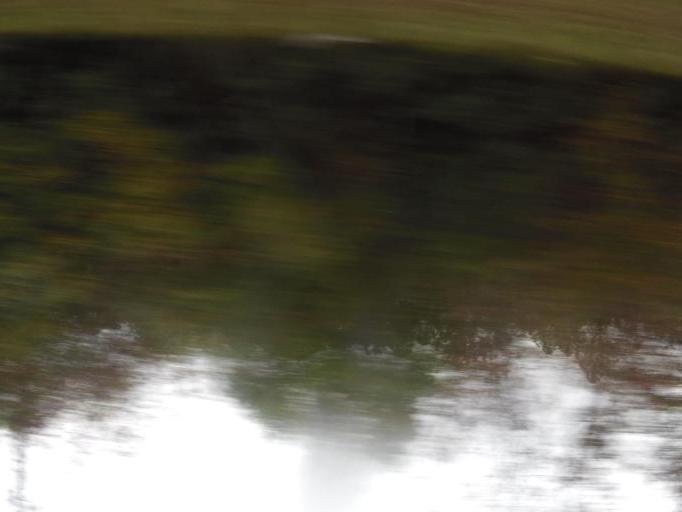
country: US
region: Georgia
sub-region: Charlton County
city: Folkston
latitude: 30.8736
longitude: -82.0464
